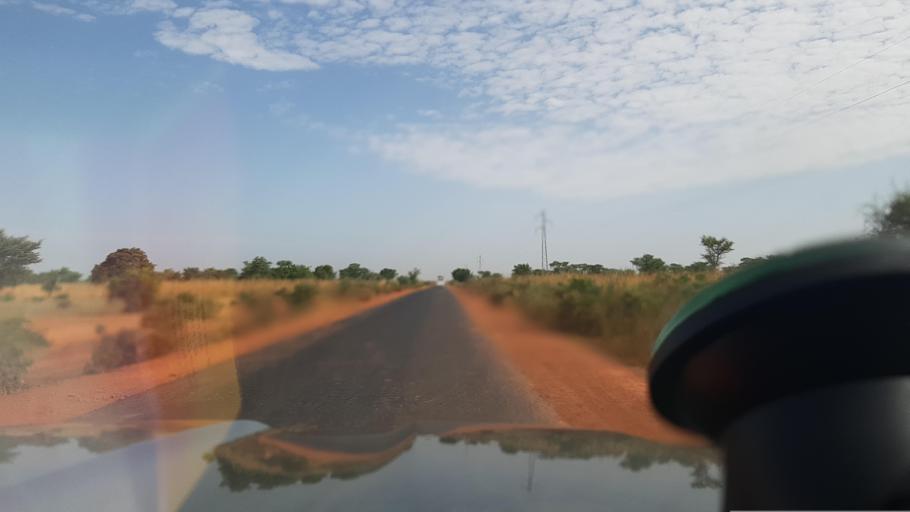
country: ML
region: Segou
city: Segou
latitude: 13.5364
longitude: -6.1240
